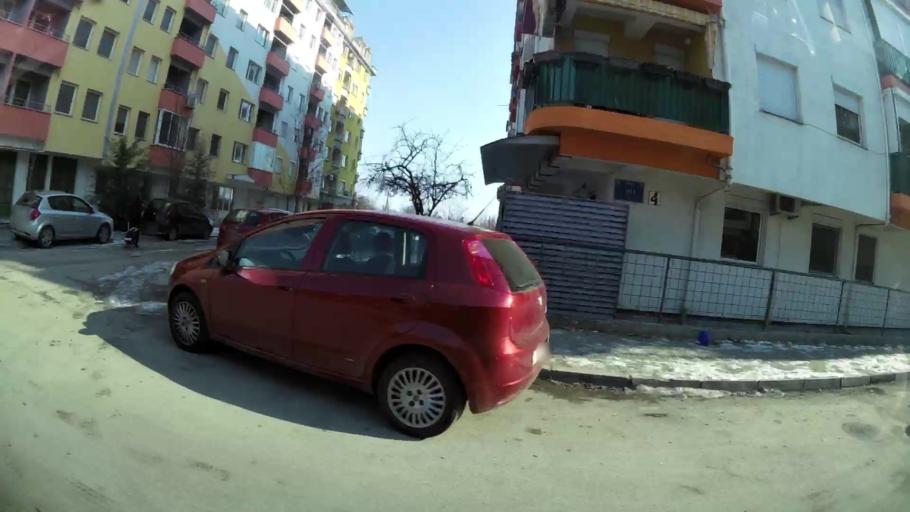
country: MK
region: Kisela Voda
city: Usje
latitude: 41.9767
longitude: 21.4464
